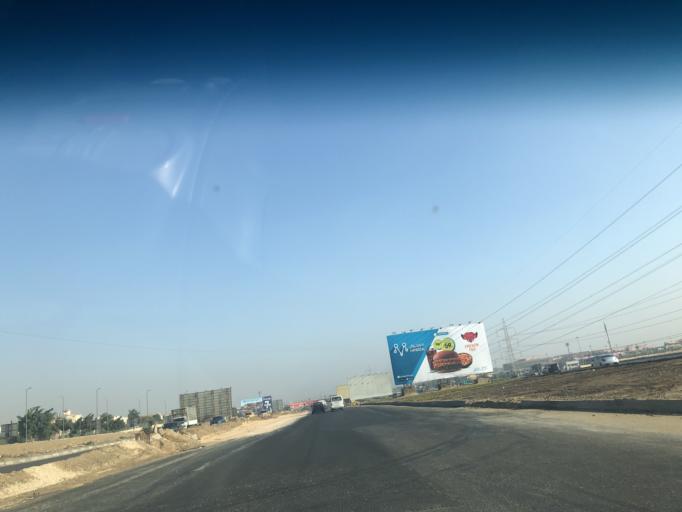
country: EG
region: Al Jizah
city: Madinat Sittah Uktubar
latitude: 29.9727
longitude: 31.0060
